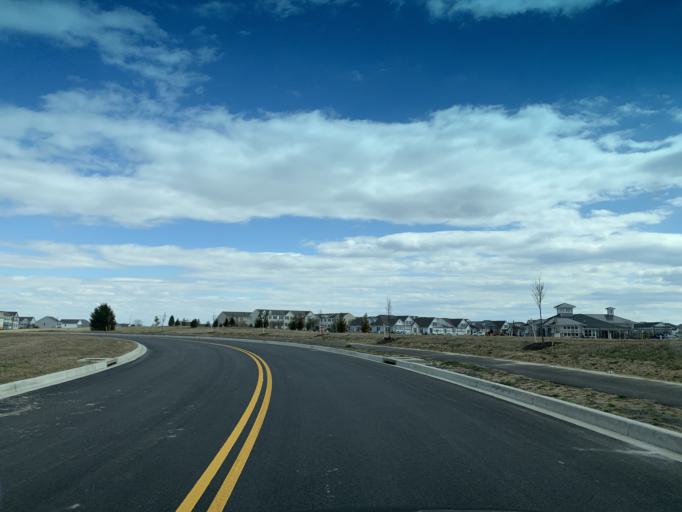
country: US
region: Maryland
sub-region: Queen Anne's County
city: Stevensville
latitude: 38.9730
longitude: -76.3254
